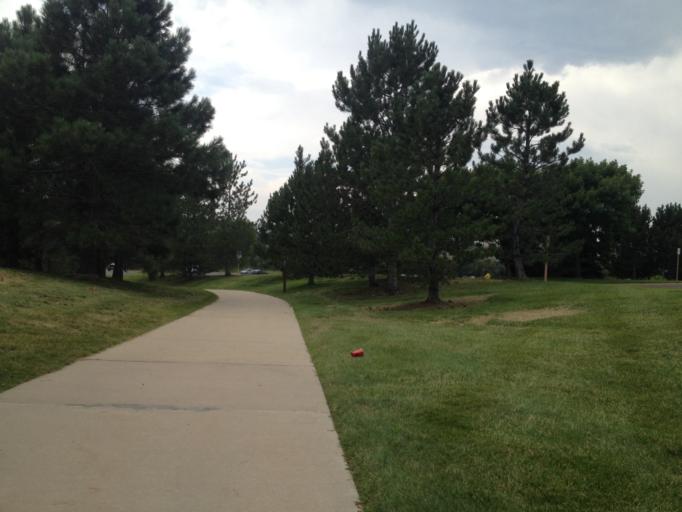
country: US
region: Colorado
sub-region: Boulder County
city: Superior
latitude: 39.9340
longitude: -105.1295
